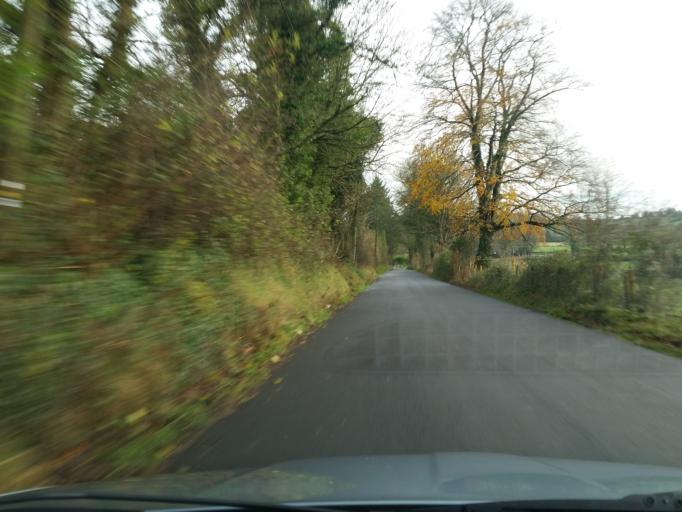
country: GB
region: Northern Ireland
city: Lisnaskea
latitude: 54.2268
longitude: -7.3497
